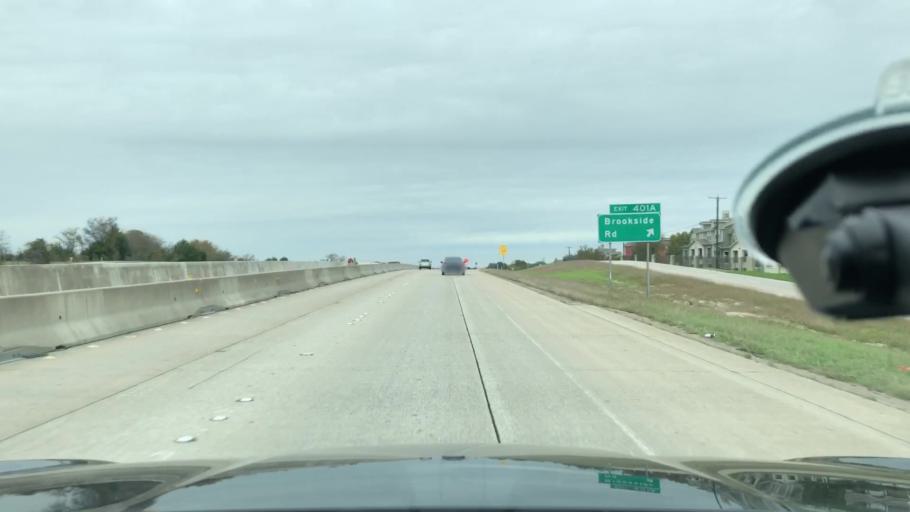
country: US
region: Texas
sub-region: Ellis County
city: Waxahachie
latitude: 32.3894
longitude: -96.8686
